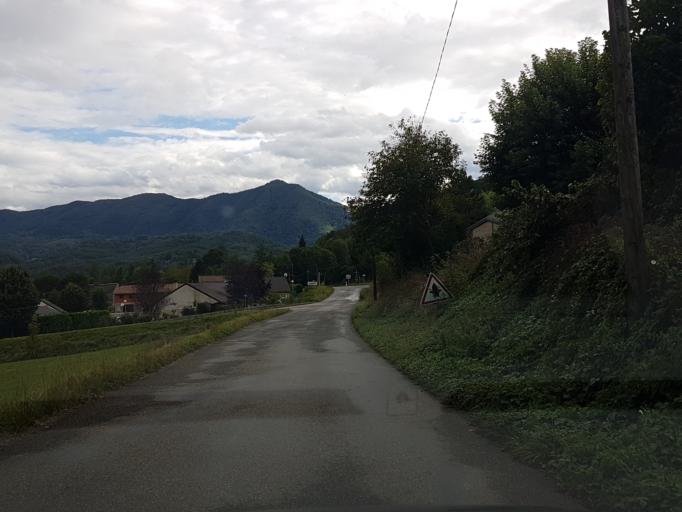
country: FR
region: Midi-Pyrenees
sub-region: Departement de l'Ariege
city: Saint-Girons
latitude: 42.8904
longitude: 1.2108
